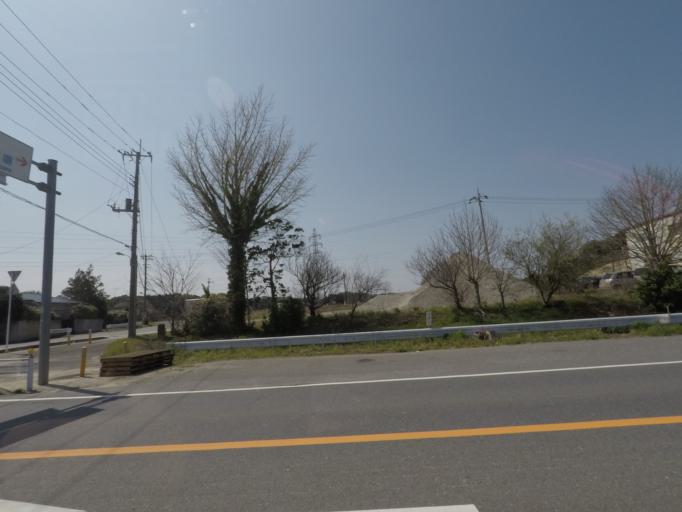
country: JP
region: Chiba
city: Narita
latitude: 35.8589
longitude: 140.2948
